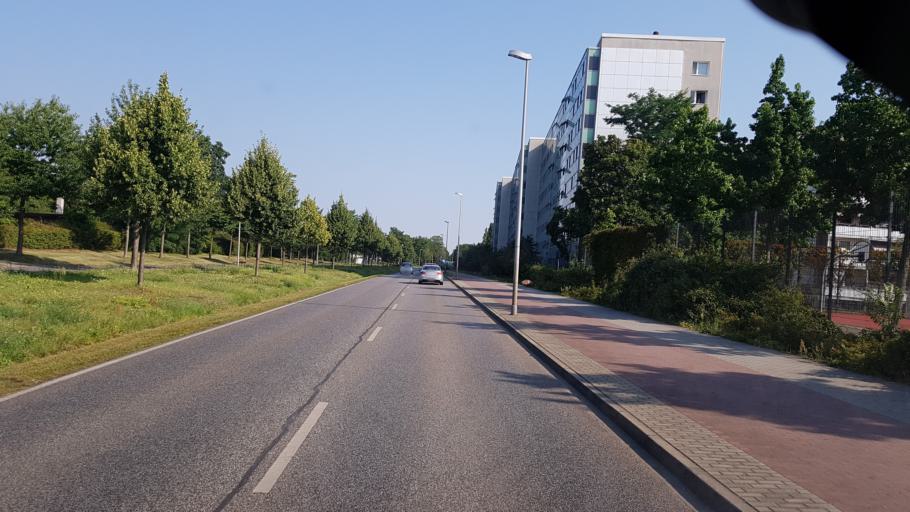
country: DE
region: Brandenburg
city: Cottbus
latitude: 51.7628
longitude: 14.3132
